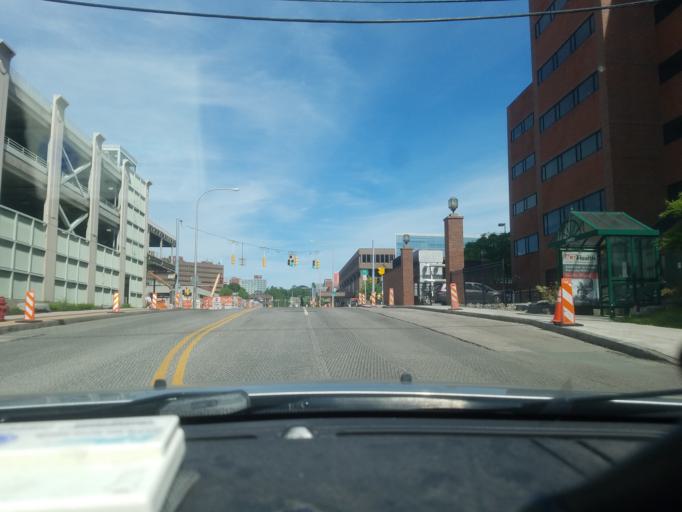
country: US
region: New York
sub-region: Onondaga County
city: Syracuse
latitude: 43.0406
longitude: -76.1375
